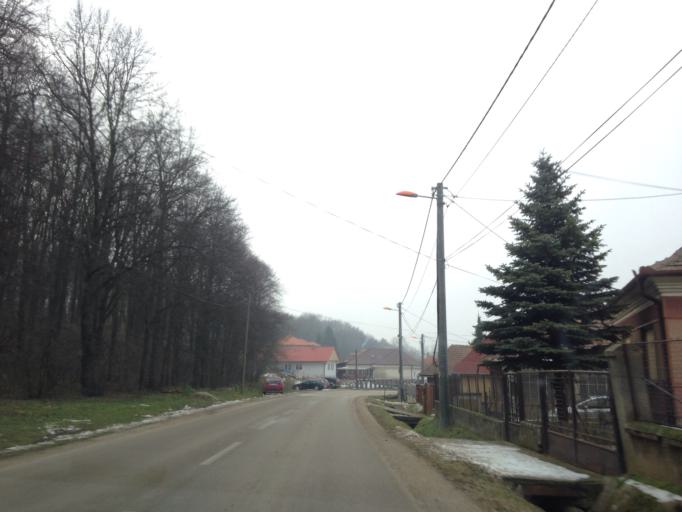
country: SK
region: Nitriansky
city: Svodin
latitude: 48.0054
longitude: 18.3629
